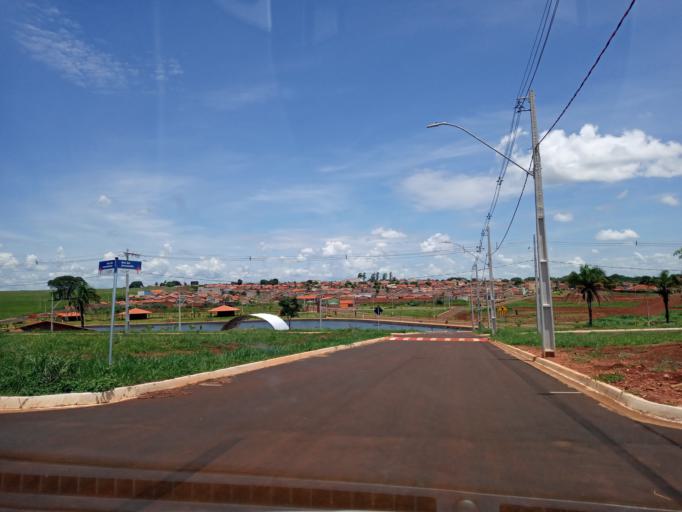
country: BR
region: Goias
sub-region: Itumbiara
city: Itumbiara
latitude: -18.4320
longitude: -49.1816
